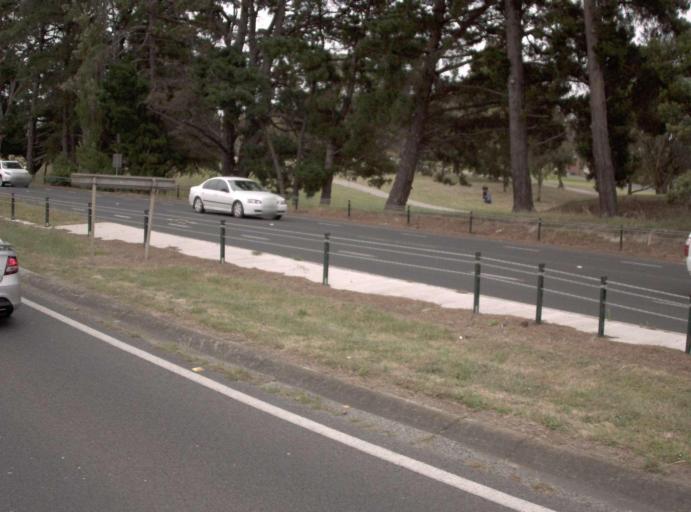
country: AU
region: Victoria
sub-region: Latrobe
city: Traralgon
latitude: -38.2056
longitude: 146.5094
